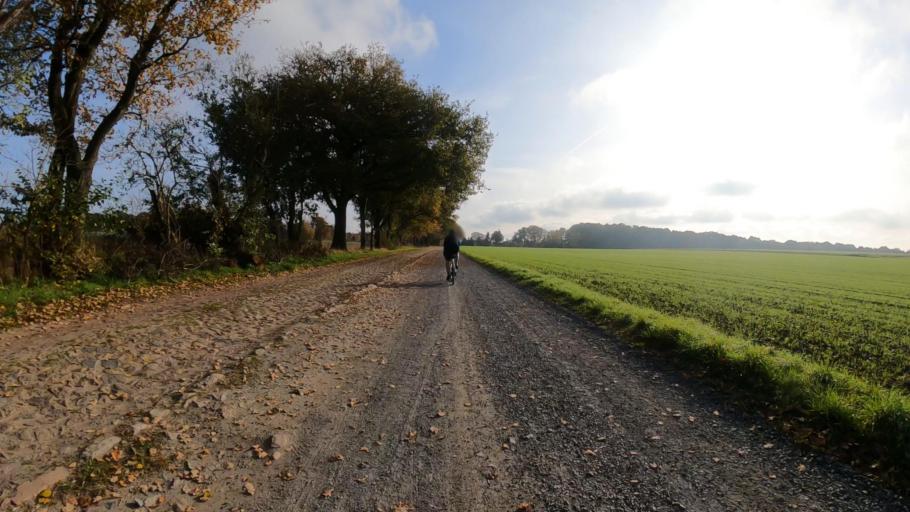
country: DE
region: Lower Saxony
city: Buchholz in der Nordheide
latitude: 53.3364
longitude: 9.8373
